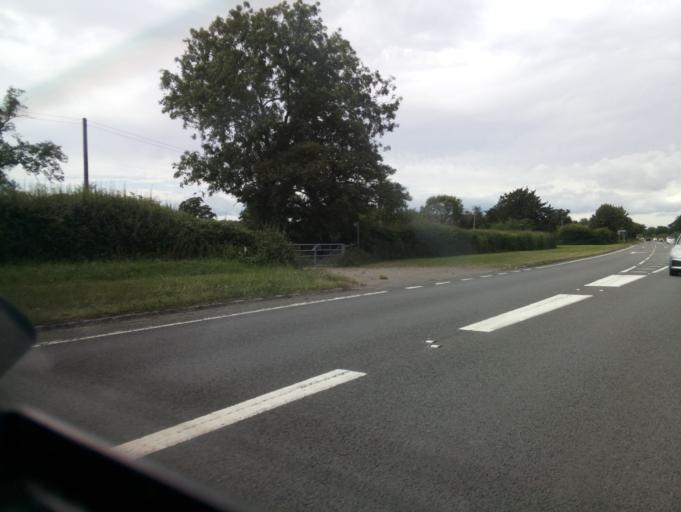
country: GB
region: England
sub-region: Somerset
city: Yeovil
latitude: 50.8721
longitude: -2.5969
